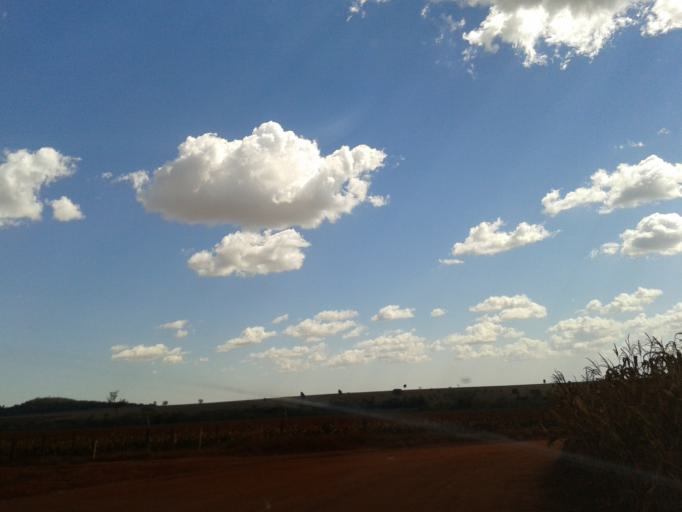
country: BR
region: Minas Gerais
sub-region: Capinopolis
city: Capinopolis
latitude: -18.6196
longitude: -49.4946
